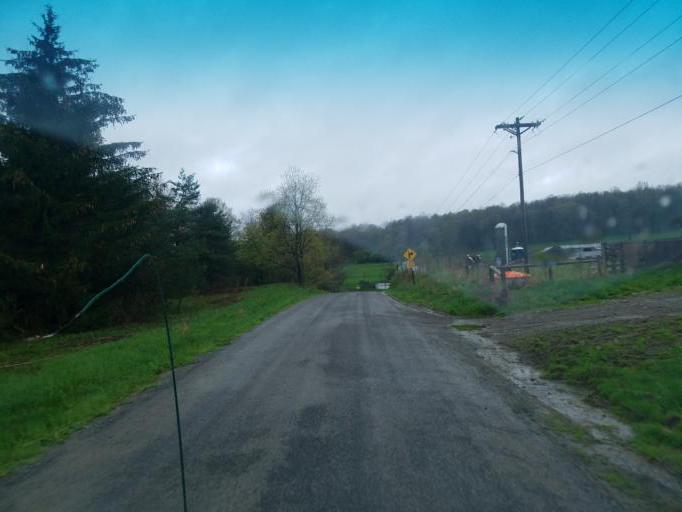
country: US
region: Pennsylvania
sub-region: Tioga County
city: Westfield
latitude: 41.9820
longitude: -77.6948
